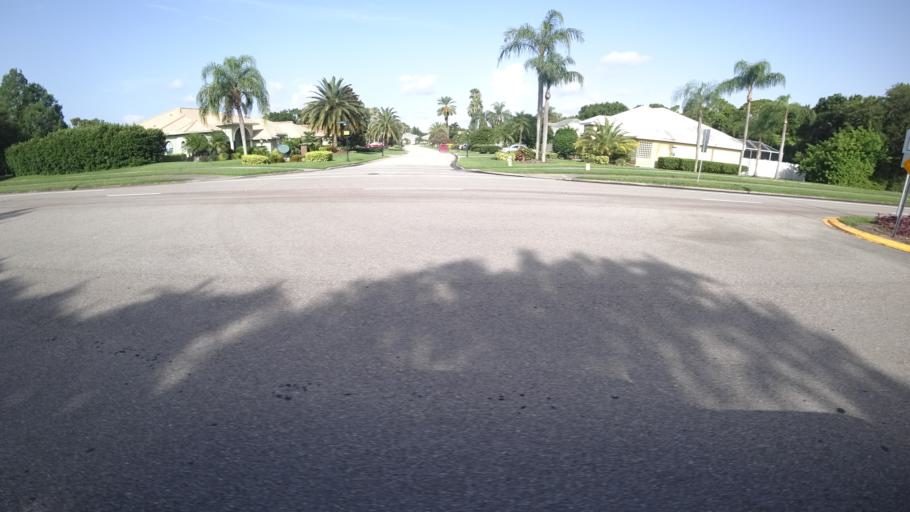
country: US
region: Florida
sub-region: Sarasota County
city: Desoto Lakes
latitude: 27.4344
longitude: -82.4690
